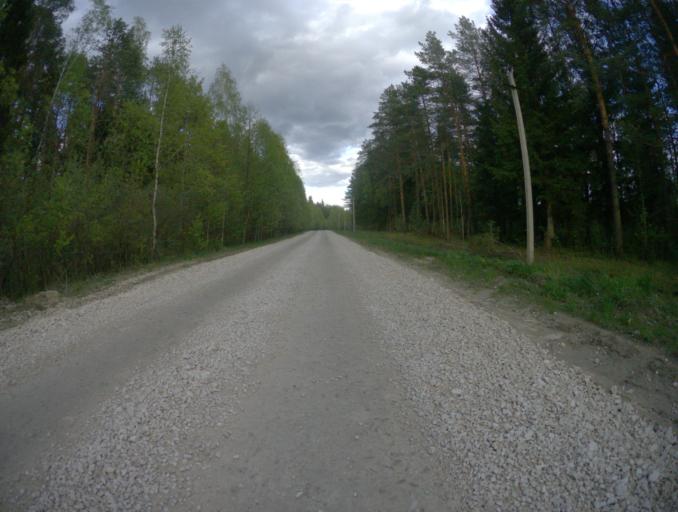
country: RU
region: Vladimir
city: Gusevskiy
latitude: 55.7216
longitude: 40.5719
